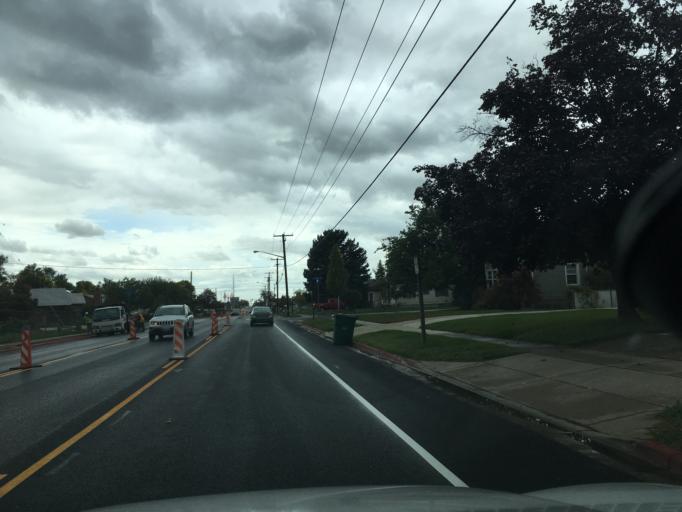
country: US
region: Utah
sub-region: Davis County
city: Layton
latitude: 41.0601
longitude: -111.9540
